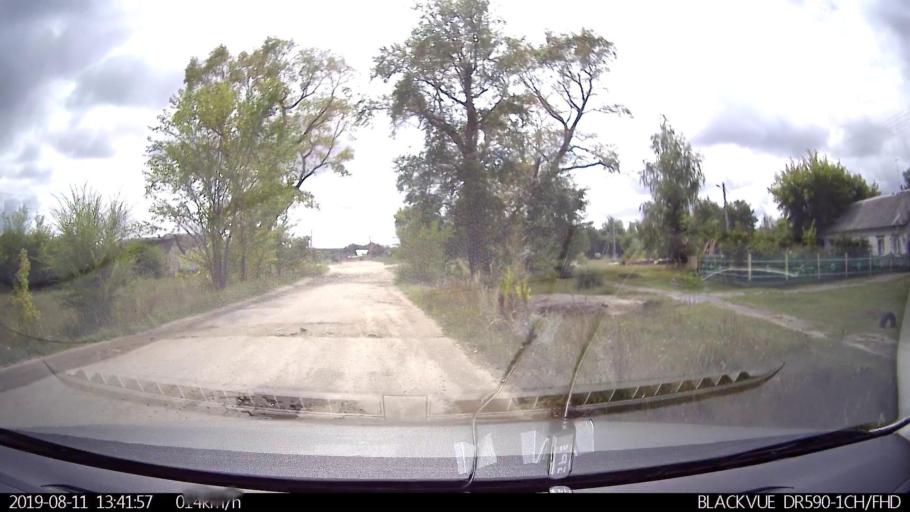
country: RU
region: Ulyanovsk
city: Ignatovka
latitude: 53.8568
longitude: 47.5754
